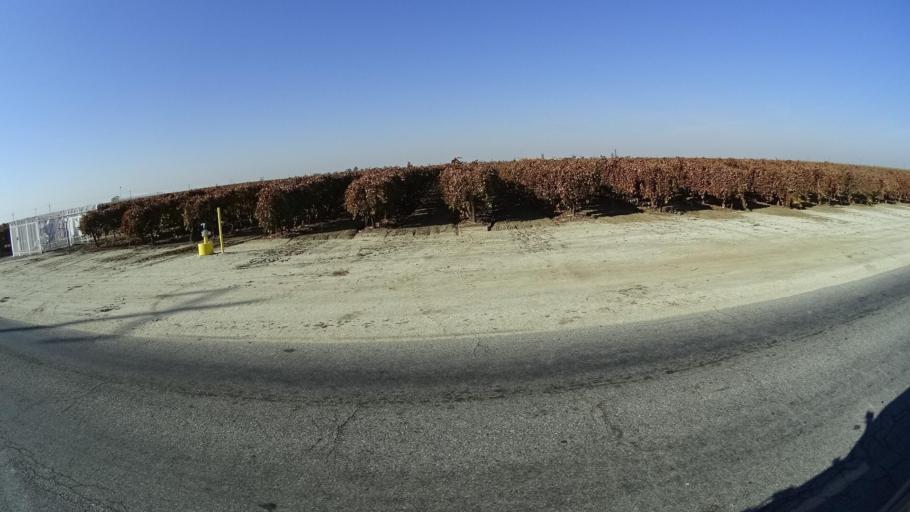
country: US
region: California
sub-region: Kern County
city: Delano
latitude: 35.7640
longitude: -119.2052
